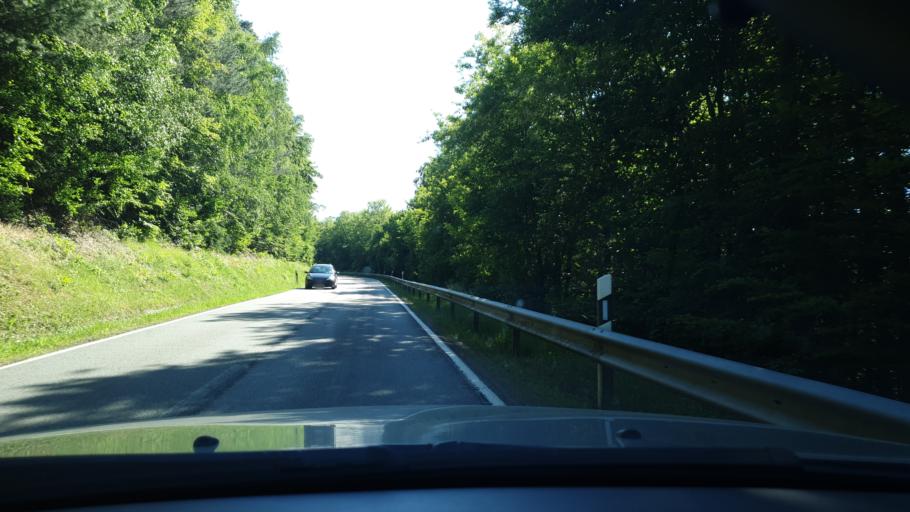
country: DE
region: Rheinland-Pfalz
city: Kaiserslautern
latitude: 49.4656
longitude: 7.7828
